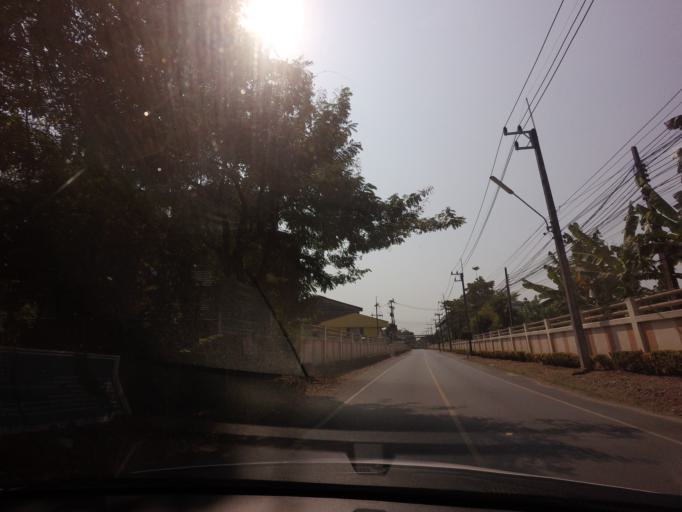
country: TH
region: Nakhon Pathom
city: Sam Phran
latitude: 13.7758
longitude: 100.2374
